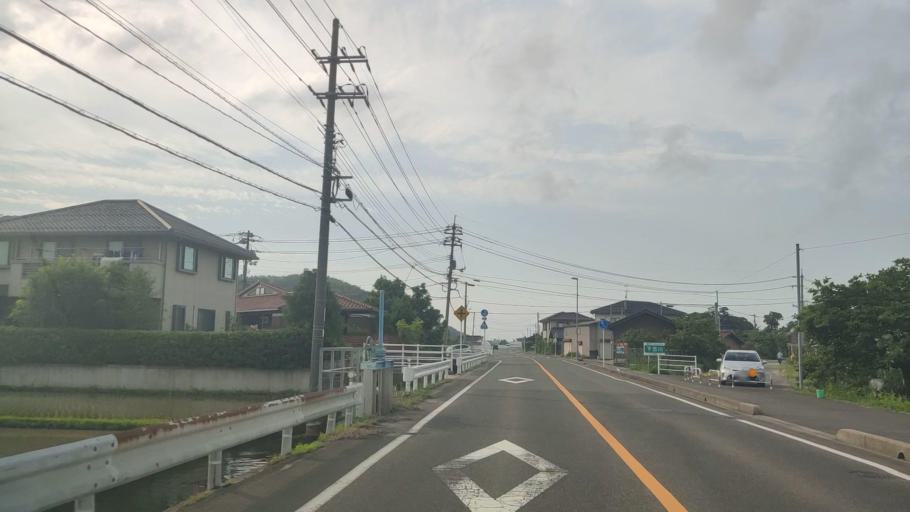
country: JP
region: Tottori
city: Kurayoshi
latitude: 35.4628
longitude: 133.8335
